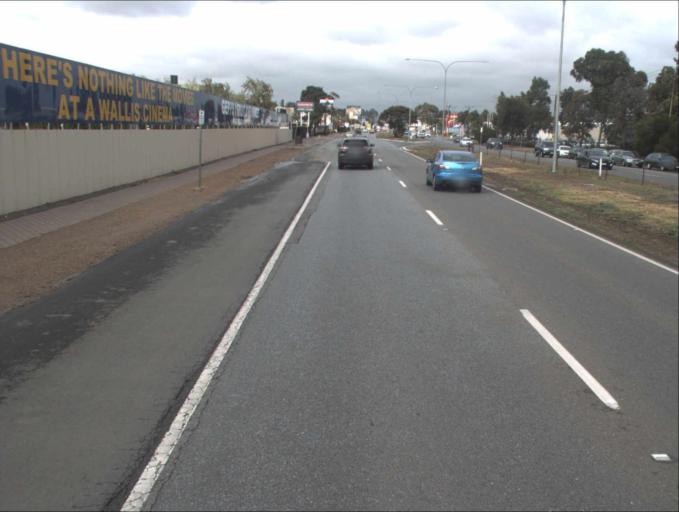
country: AU
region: South Australia
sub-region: Port Adelaide Enfield
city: Enfield
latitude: -34.8429
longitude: 138.5999
